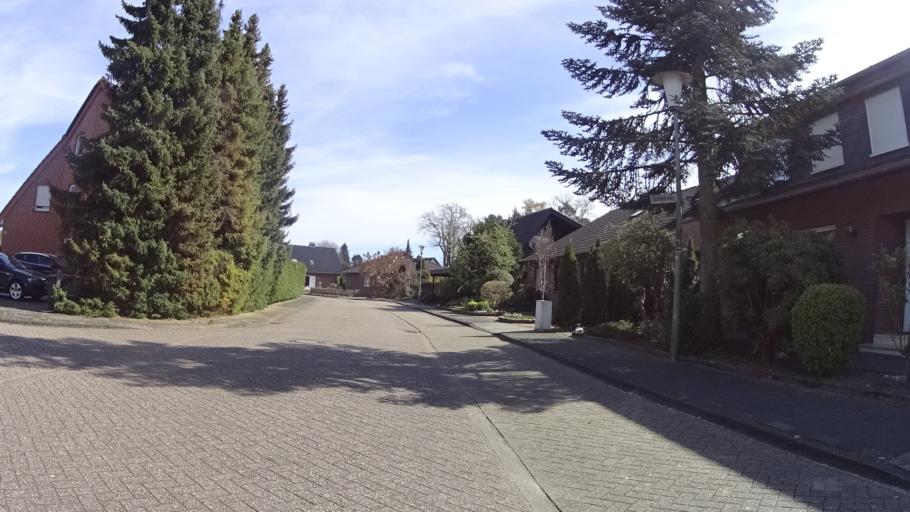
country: DE
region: North Rhine-Westphalia
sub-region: Regierungsbezirk Munster
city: Dreierwalde
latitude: 52.2810
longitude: 7.4756
